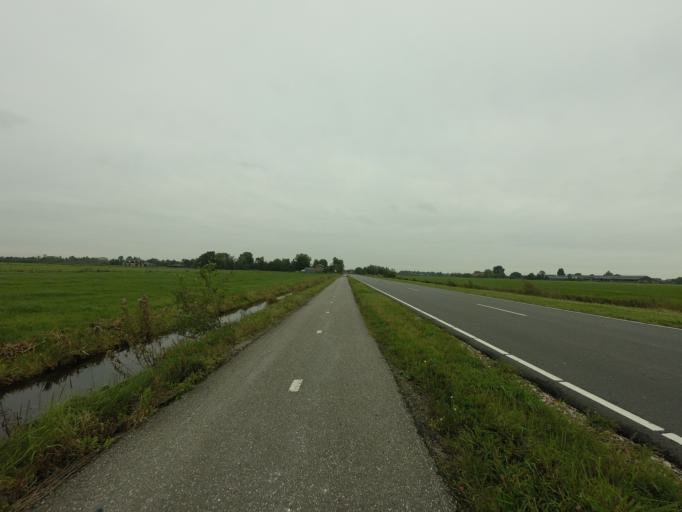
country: NL
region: Utrecht
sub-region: Gemeente Woerden
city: Woerden
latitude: 52.1436
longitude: 4.8603
